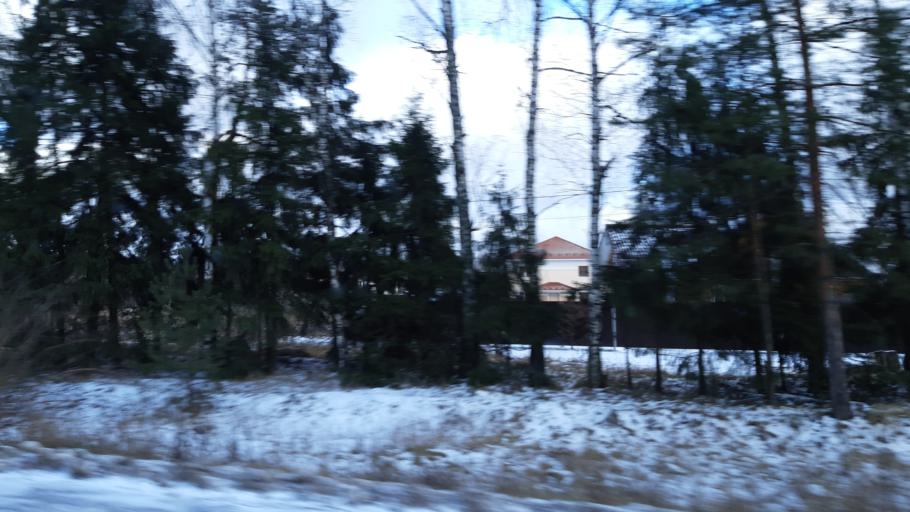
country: RU
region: Moskovskaya
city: Noginsk-9
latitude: 55.9566
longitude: 38.5467
